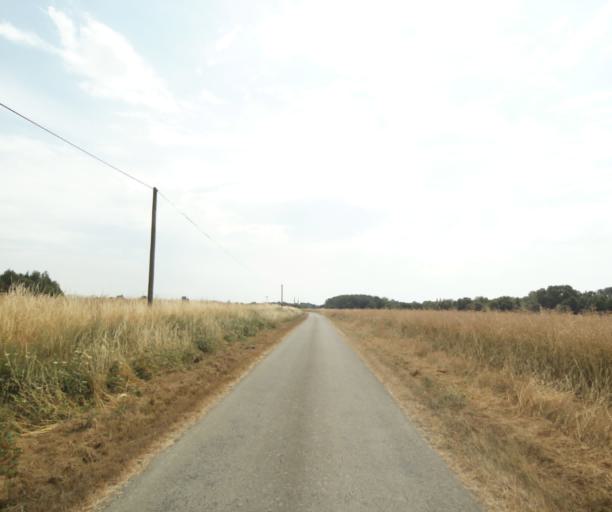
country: FR
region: Centre
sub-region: Departement d'Eure-et-Loir
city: La Bazoche-Gouet
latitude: 48.1847
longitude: 0.9512
